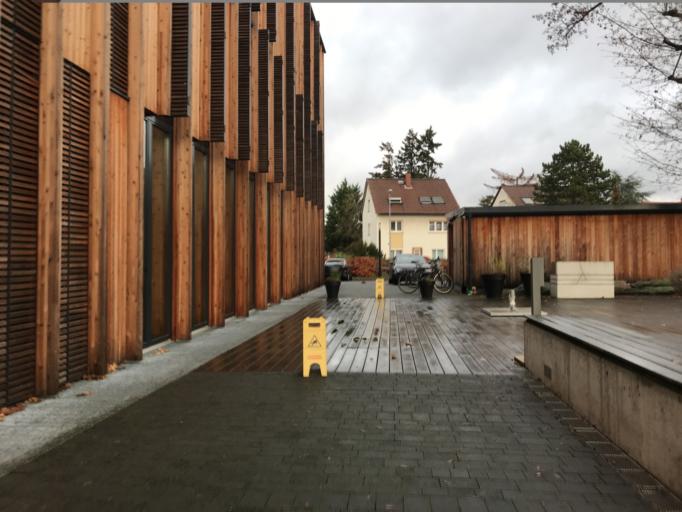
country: DE
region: Rheinland-Pfalz
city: Mainz
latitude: 50.0014
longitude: 8.2375
